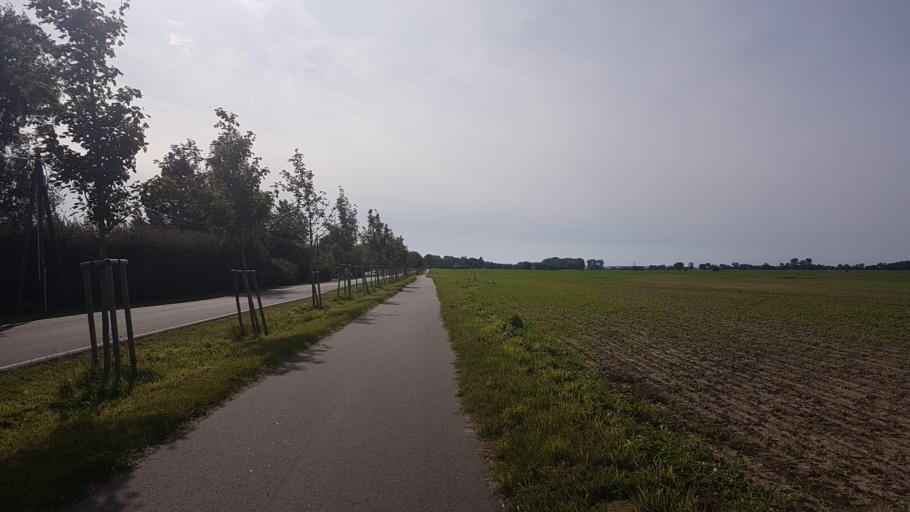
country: DE
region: Mecklenburg-Vorpommern
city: Gingst
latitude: 54.4565
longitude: 13.1671
